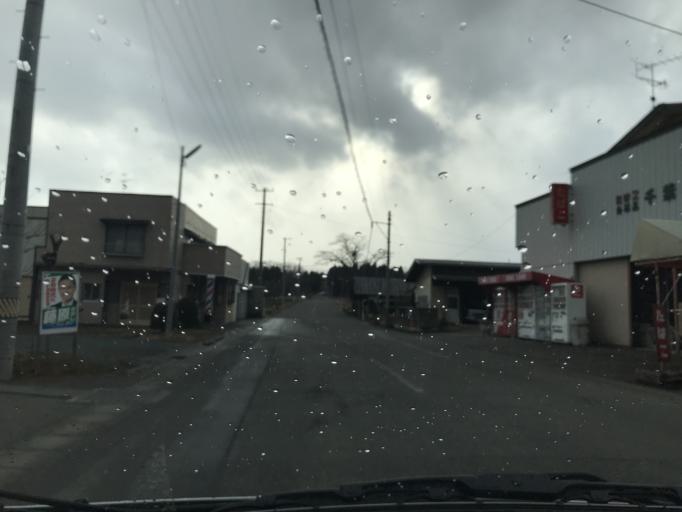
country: JP
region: Iwate
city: Mizusawa
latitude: 39.1000
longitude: 141.0306
